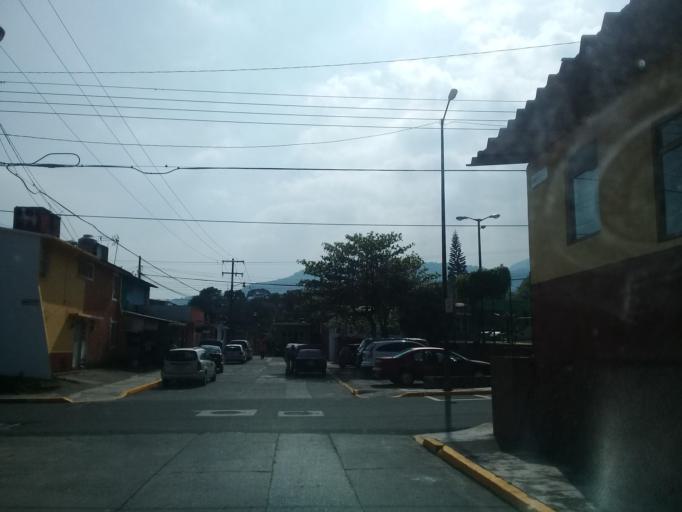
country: MX
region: Veracruz
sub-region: Mariano Escobedo
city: Palmira
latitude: 18.8706
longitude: -97.1051
